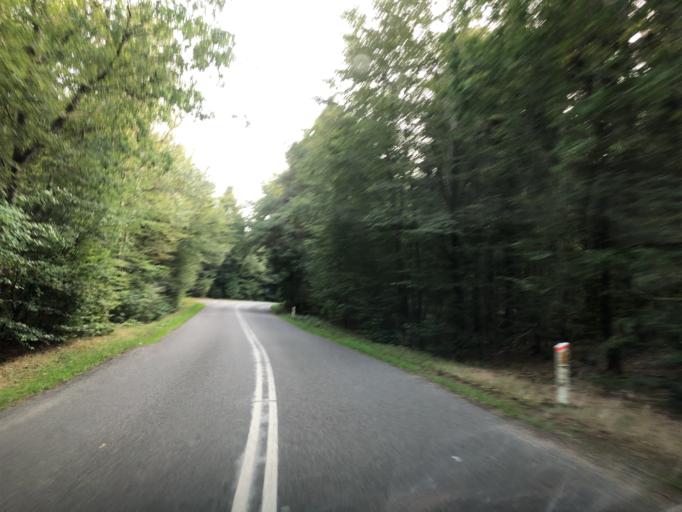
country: DK
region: Central Jutland
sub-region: Ringkobing-Skjern Kommune
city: Videbaek
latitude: 56.0637
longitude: 8.6876
